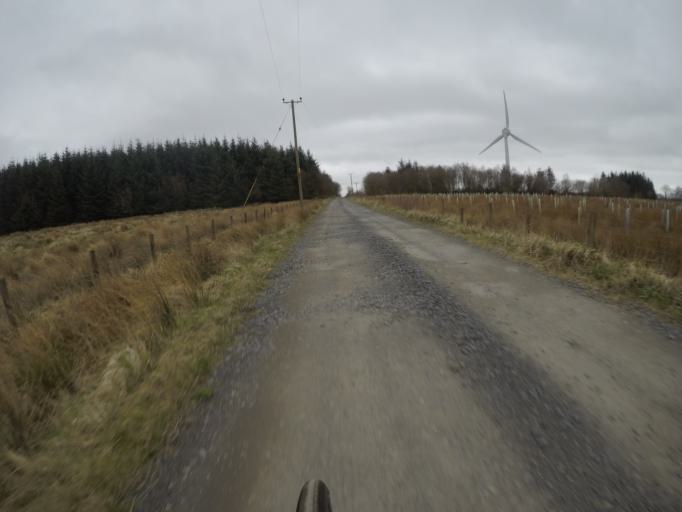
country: GB
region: Scotland
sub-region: East Ayrshire
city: Newmilns
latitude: 55.6283
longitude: -4.3424
